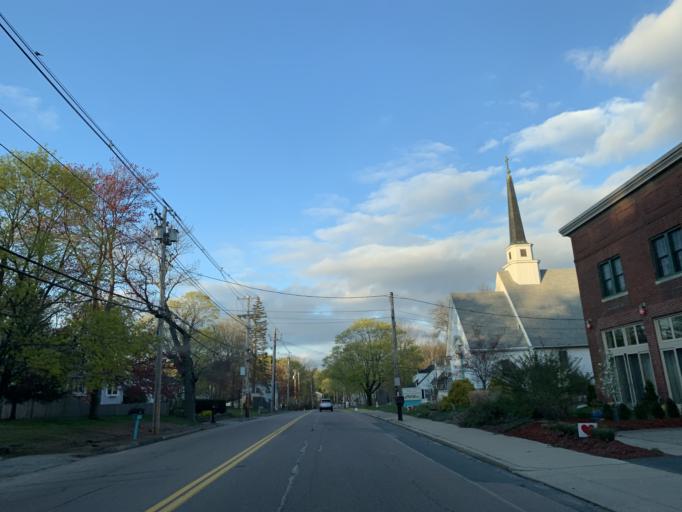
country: US
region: Massachusetts
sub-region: Bristol County
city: North Seekonk
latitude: 41.9231
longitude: -71.3529
